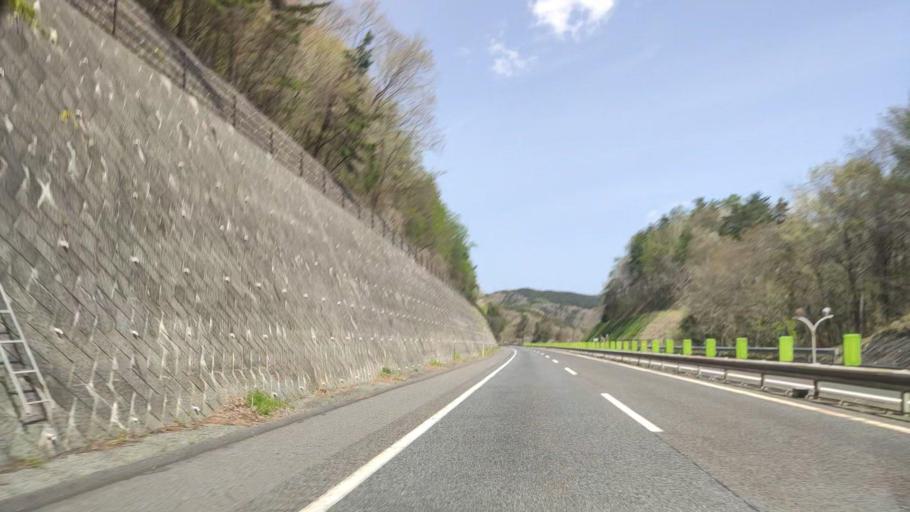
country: JP
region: Aomori
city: Hachinohe
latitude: 40.3553
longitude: 141.4493
